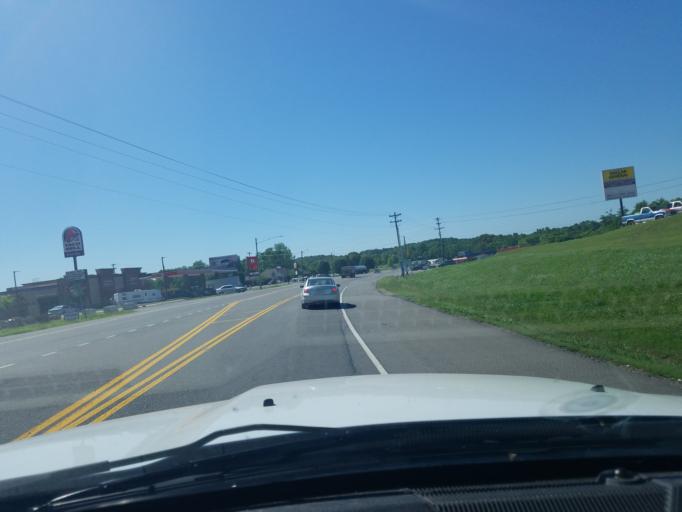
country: US
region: Tennessee
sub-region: Sumner County
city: Westmoreland
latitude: 36.5543
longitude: -86.2375
